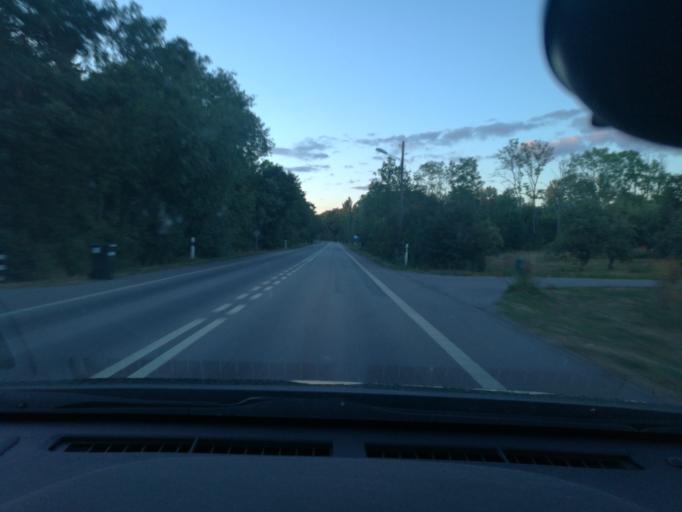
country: SE
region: Kalmar
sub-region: Borgholms Kommun
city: Borgholm
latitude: 56.7658
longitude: 16.5636
